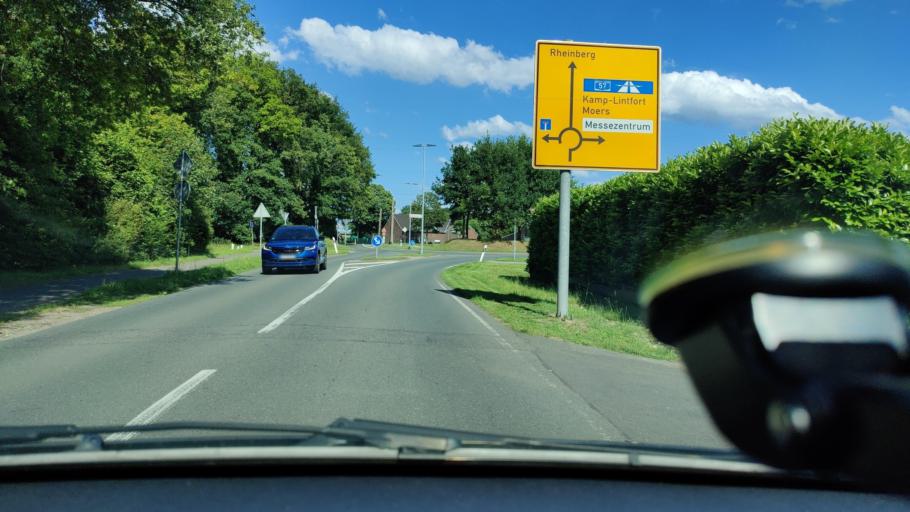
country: DE
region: North Rhine-Westphalia
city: Rheinberg
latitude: 51.5511
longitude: 6.5690
